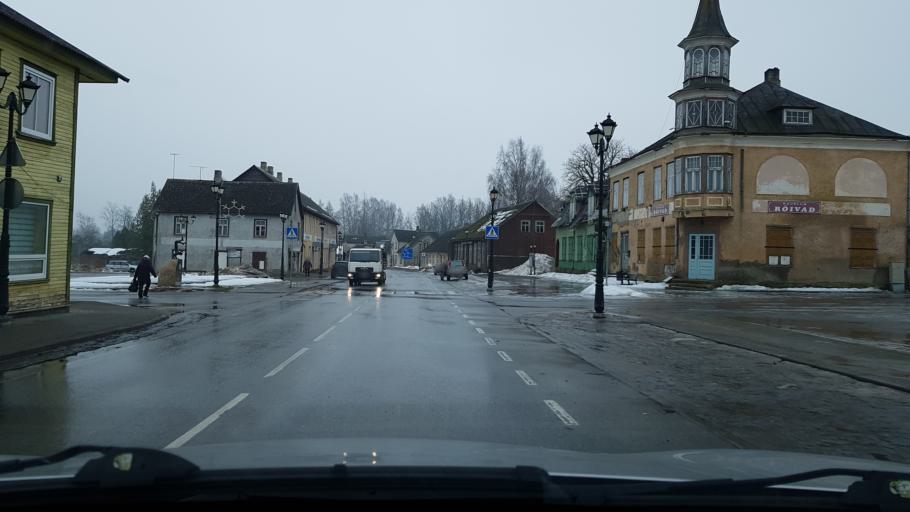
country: EE
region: Valgamaa
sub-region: Torva linn
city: Torva
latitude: 58.2364
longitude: 25.8604
